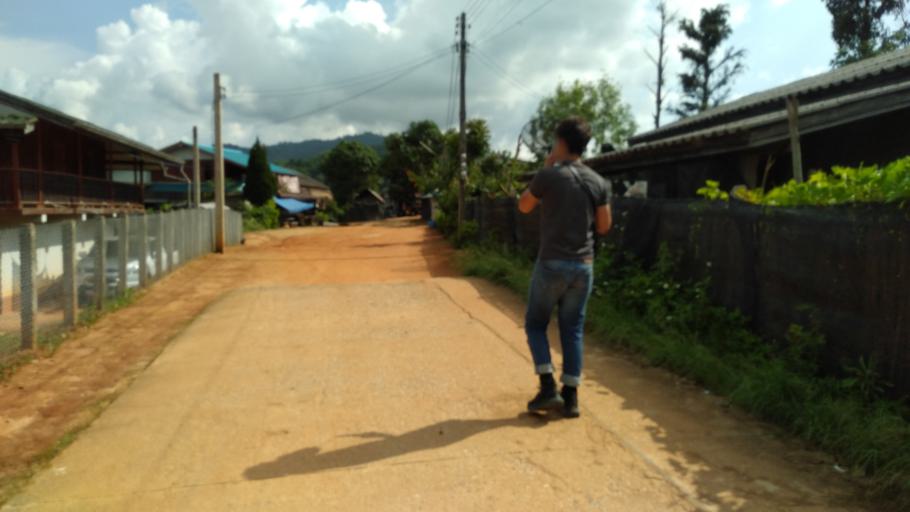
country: TH
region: Chiang Mai
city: Phrao
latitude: 19.5100
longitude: 99.3380
